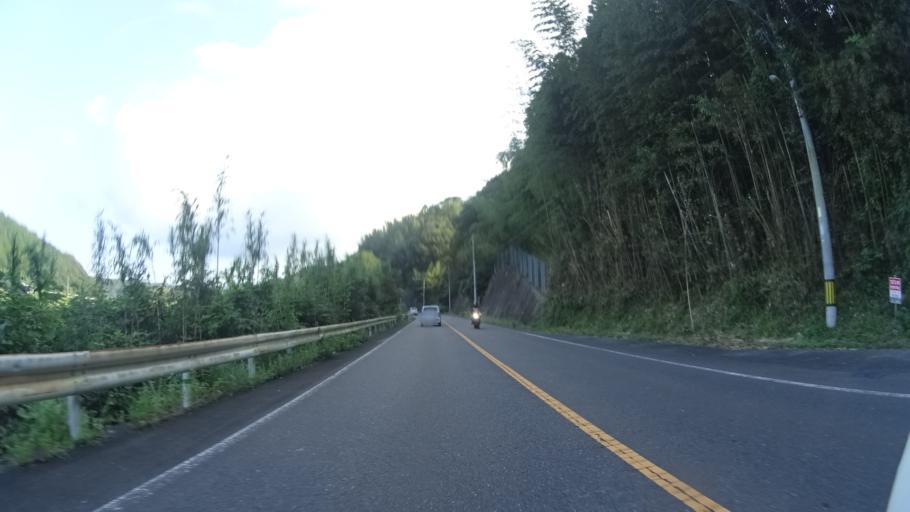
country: JP
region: Oita
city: Bungo-Takada-shi
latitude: 33.4267
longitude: 131.3735
